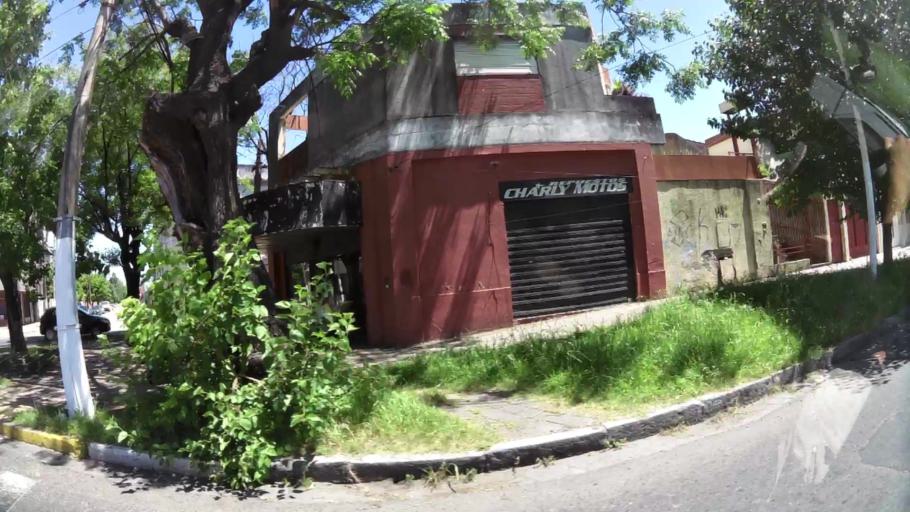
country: AR
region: Buenos Aires
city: Caseros
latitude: -34.5993
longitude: -58.5540
